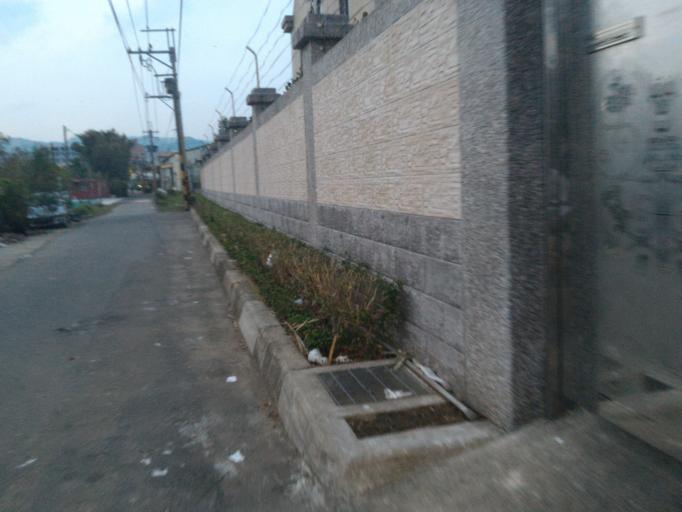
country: TW
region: Taipei
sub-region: Taipei
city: Banqiao
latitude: 24.9559
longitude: 121.4031
